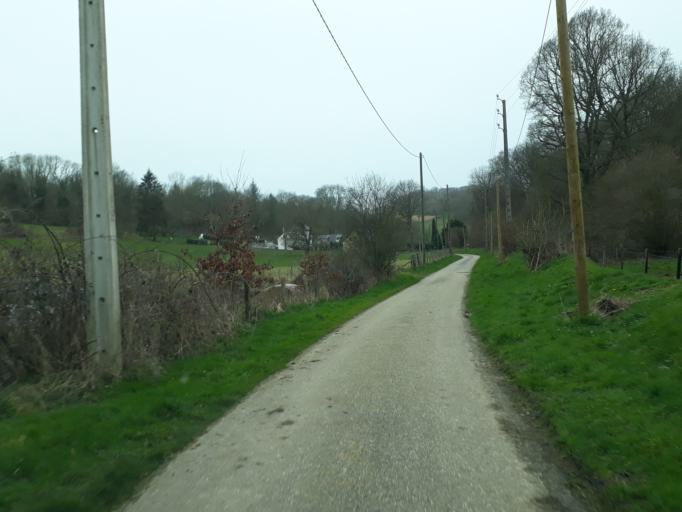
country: FR
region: Haute-Normandie
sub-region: Departement de la Seine-Maritime
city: Les Loges
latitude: 49.6698
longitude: 0.2743
